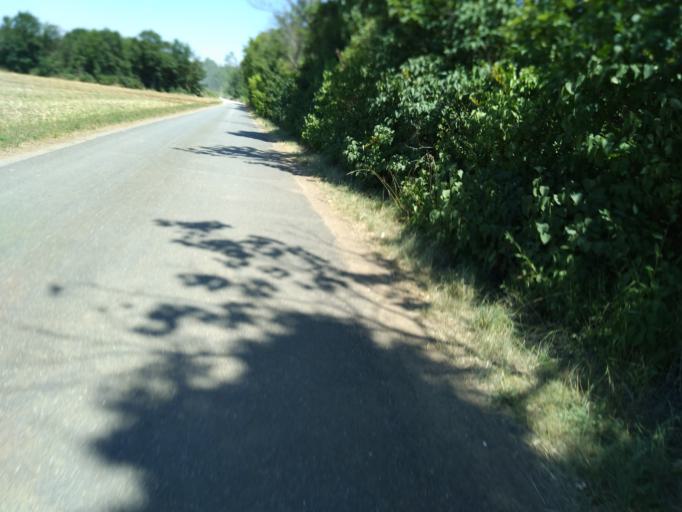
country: AT
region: Lower Austria
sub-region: Politischer Bezirk Mistelbach
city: Bockfliess
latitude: 48.3319
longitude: 16.6064
